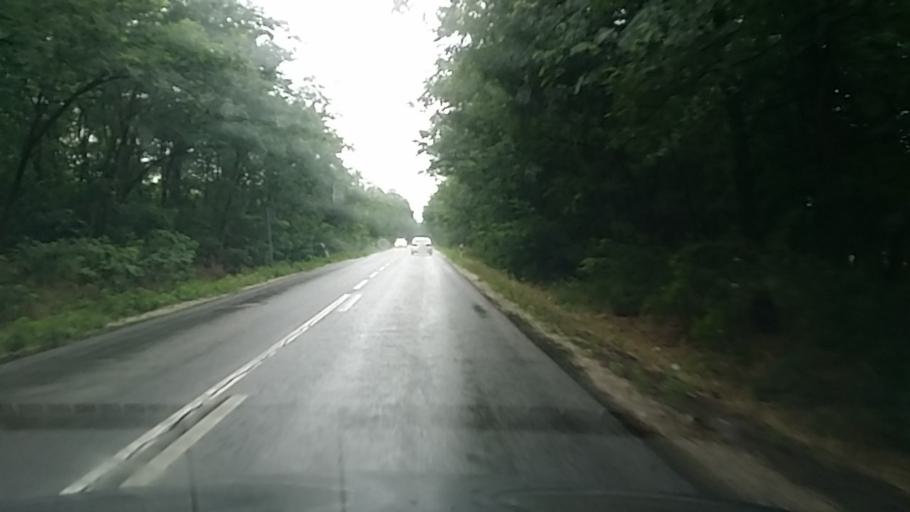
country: HU
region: Pest
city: Ullo
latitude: 47.3419
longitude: 19.3219
